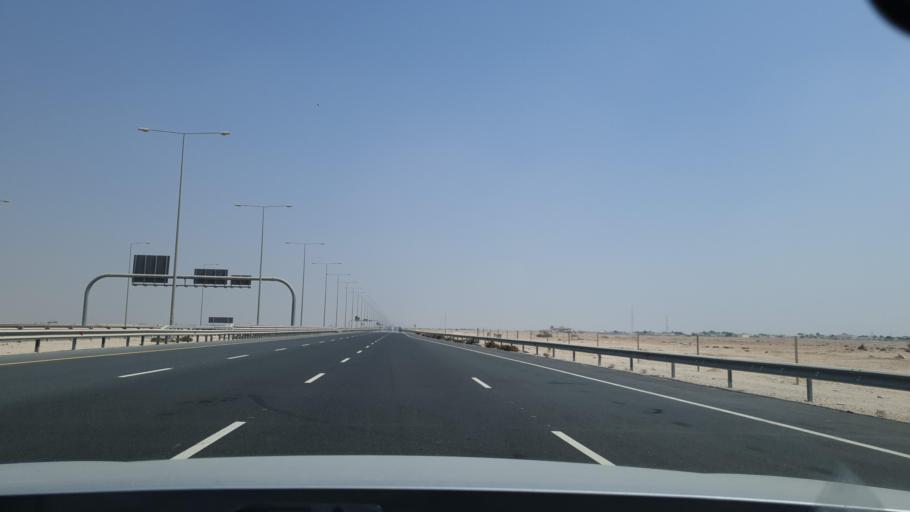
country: QA
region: Baladiyat az Za`ayin
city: Az Za`ayin
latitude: 25.6182
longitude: 51.3785
